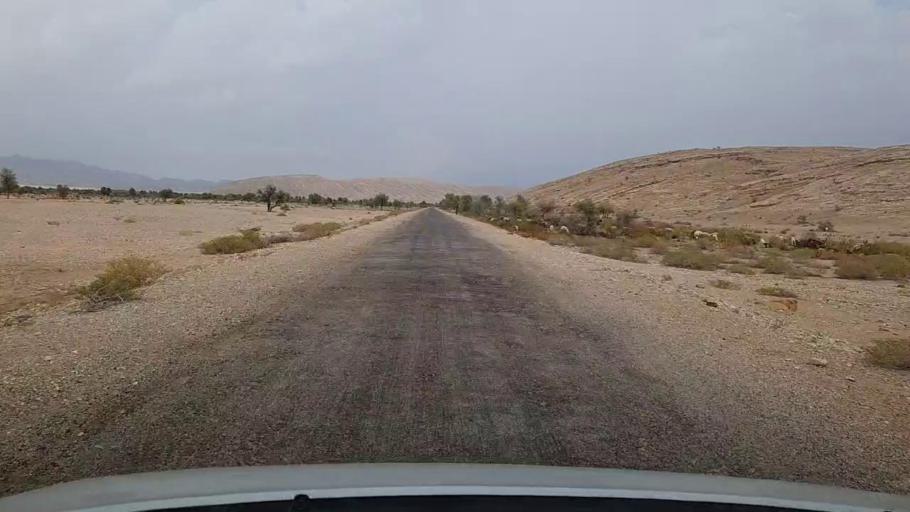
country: PK
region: Sindh
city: Sehwan
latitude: 26.2272
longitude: 67.7079
